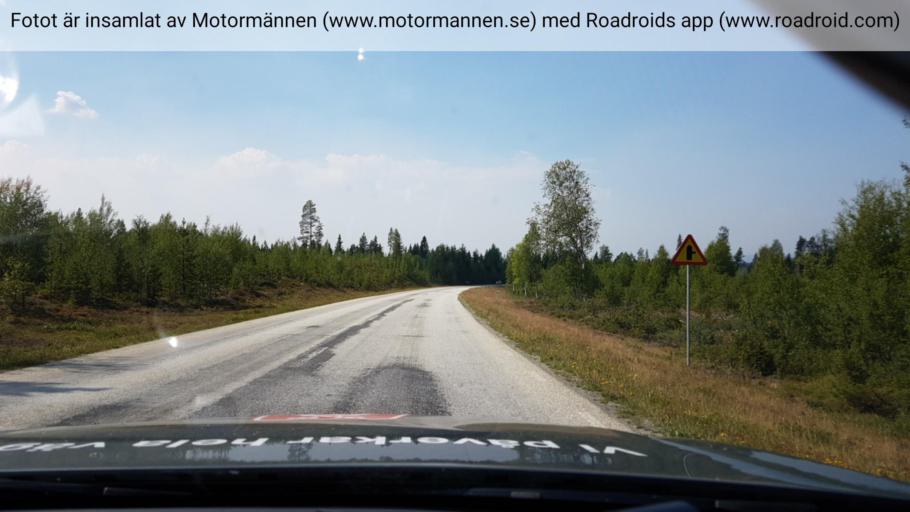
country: SE
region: Jaemtland
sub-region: Harjedalens Kommun
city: Sveg
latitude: 62.4103
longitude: 13.5872
